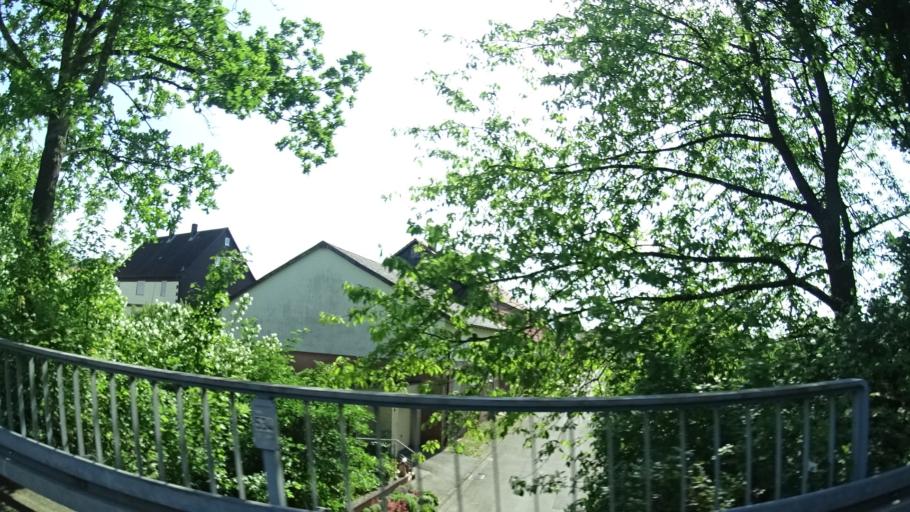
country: DE
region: Hesse
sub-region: Regierungsbezirk Giessen
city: Kirchhain
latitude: 50.8433
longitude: 8.8684
